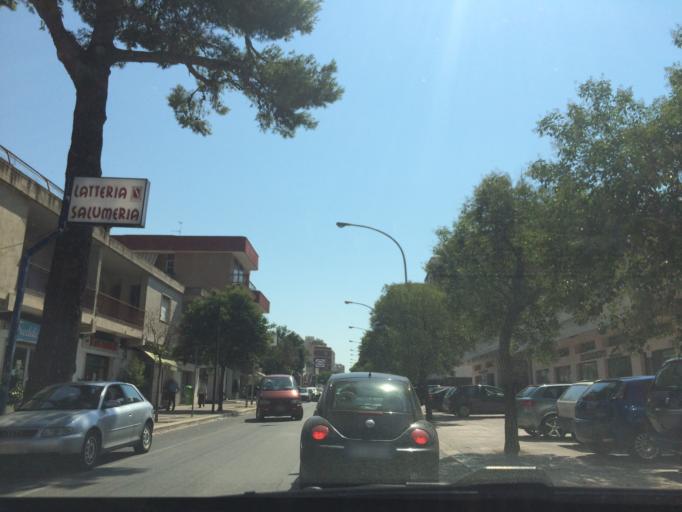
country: IT
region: Basilicate
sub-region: Provincia di Matera
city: Matera
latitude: 40.6770
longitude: 16.5926
